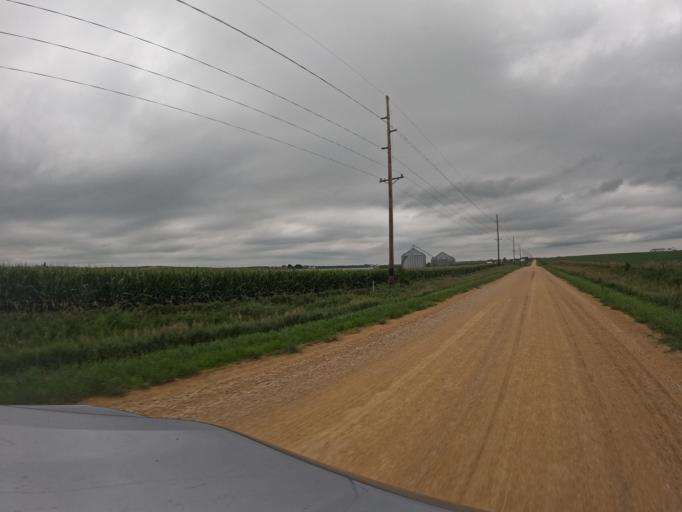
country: US
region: Iowa
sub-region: Clinton County
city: De Witt
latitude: 41.9434
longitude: -90.5870
